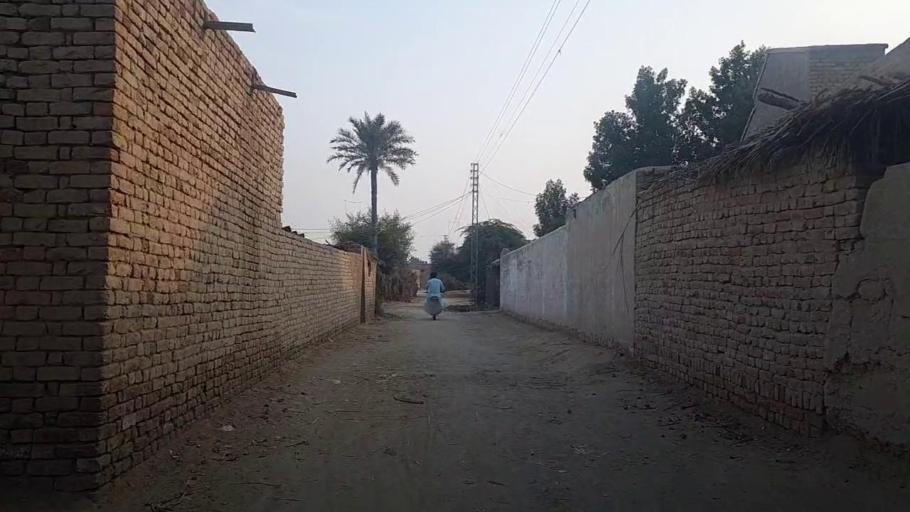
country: PK
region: Sindh
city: Kot Diji
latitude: 27.3780
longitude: 68.6655
